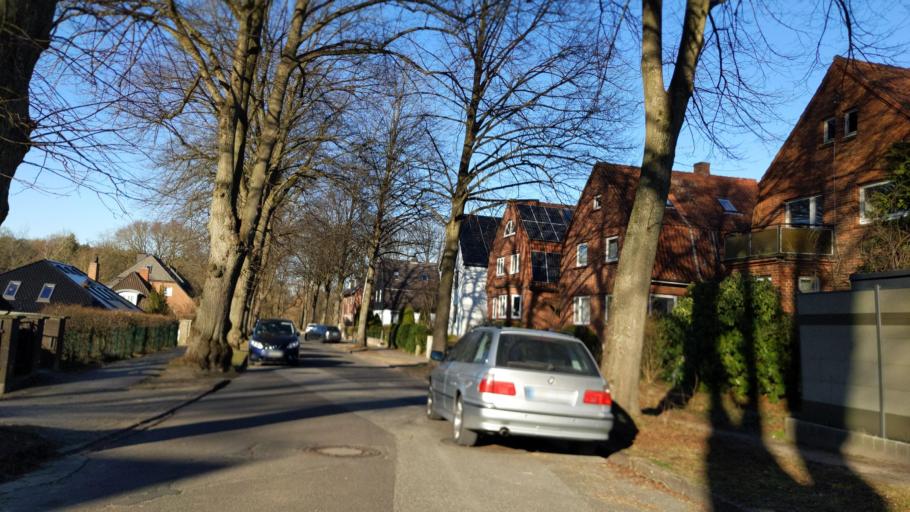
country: DE
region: Schleswig-Holstein
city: Bad Schwartau
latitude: 53.9121
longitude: 10.6892
